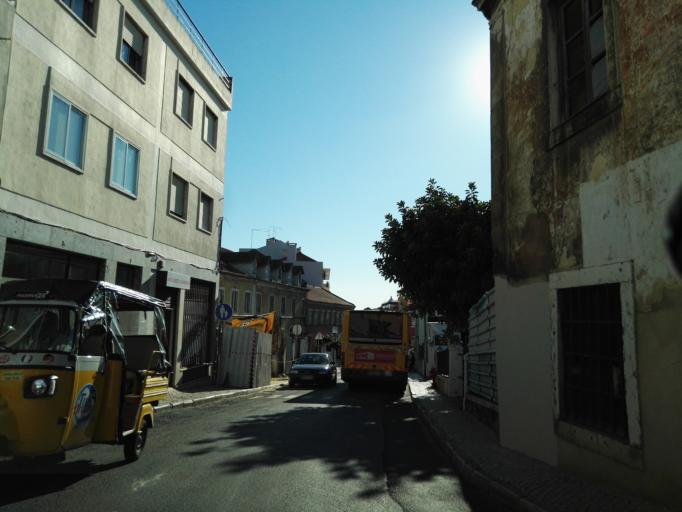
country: PT
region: Lisbon
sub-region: Lisbon
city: Lisbon
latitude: 38.7295
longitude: -9.1084
